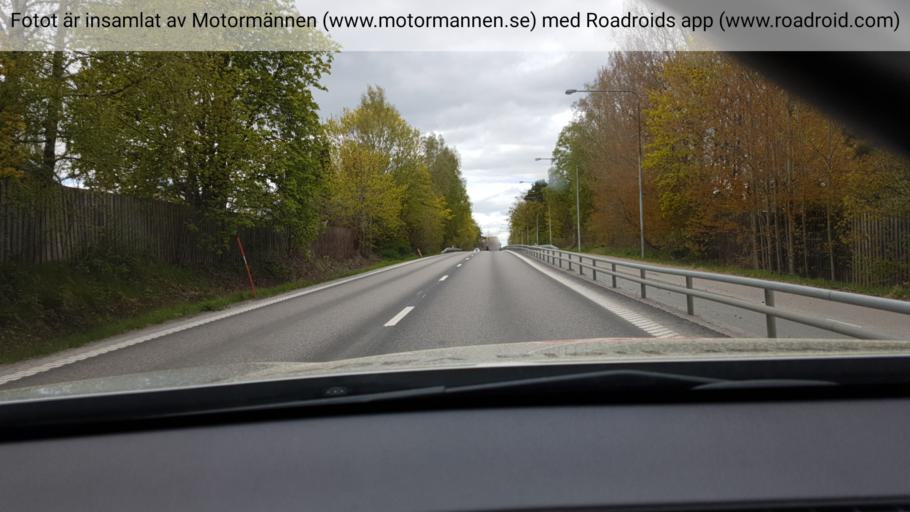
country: SE
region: Stockholm
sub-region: Tyreso Kommun
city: Bollmora
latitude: 59.2189
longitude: 18.2036
